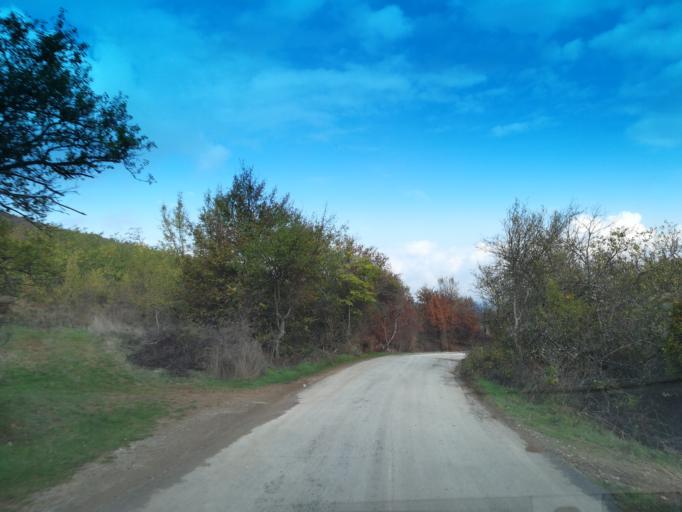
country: BG
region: Stara Zagora
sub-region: Obshtina Nikolaevo
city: Elkhovo
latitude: 42.3329
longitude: 25.4044
